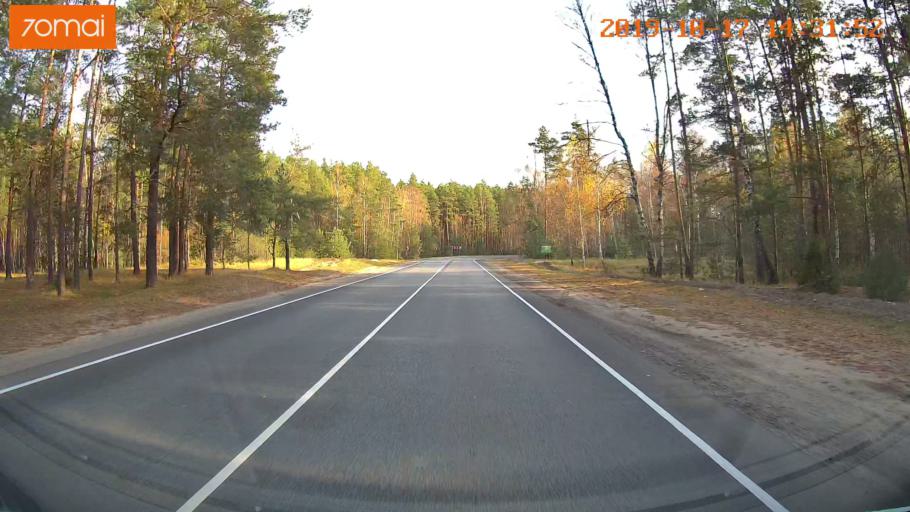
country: RU
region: Rjazan
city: Solotcha
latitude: 54.9327
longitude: 39.9722
